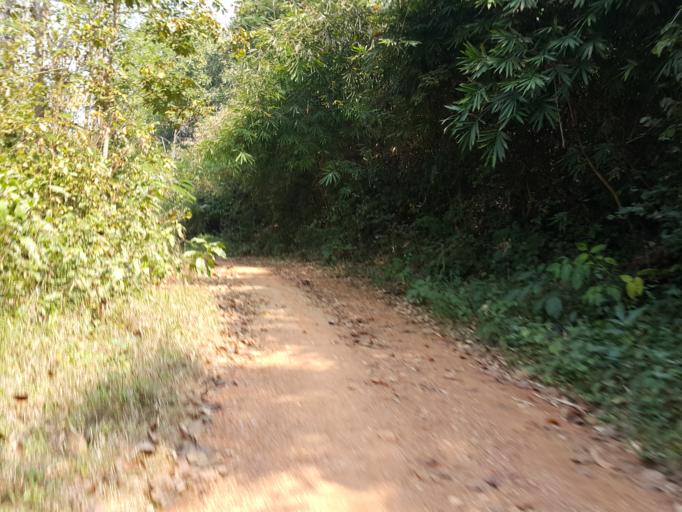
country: TH
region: Sukhothai
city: Thung Saliam
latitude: 17.3053
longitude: 99.5046
